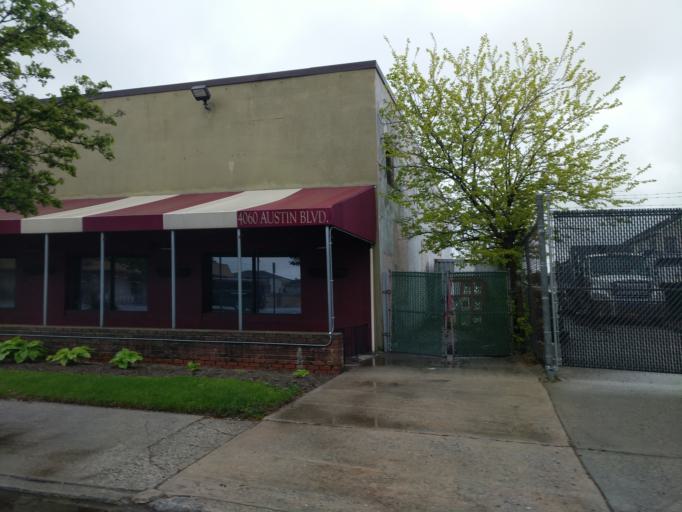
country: US
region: New York
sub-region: Nassau County
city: Barnum Island
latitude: 40.6109
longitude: -73.6452
